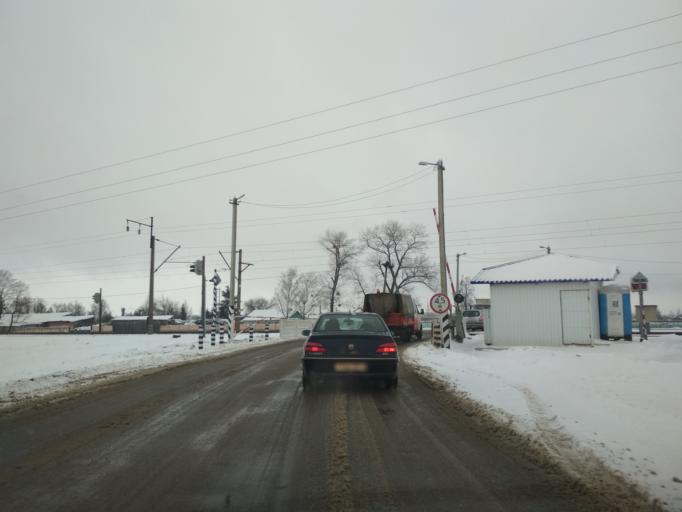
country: BY
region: Minsk
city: Mar''ina Horka
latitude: 53.4987
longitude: 28.1496
